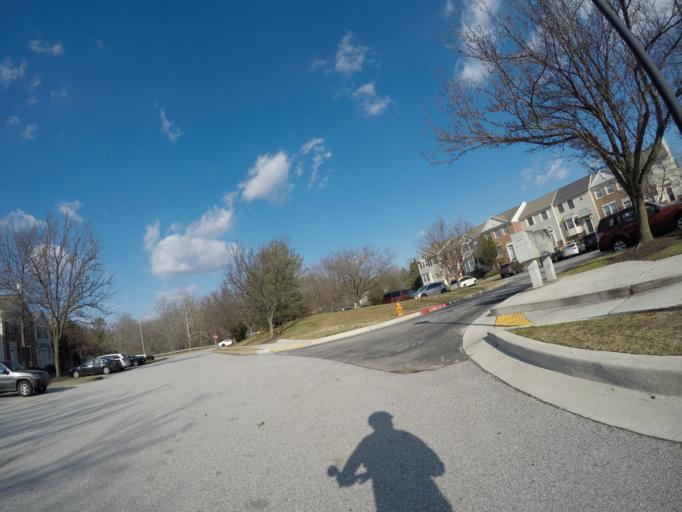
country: US
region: Maryland
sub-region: Howard County
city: Ilchester
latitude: 39.2109
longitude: -76.7876
